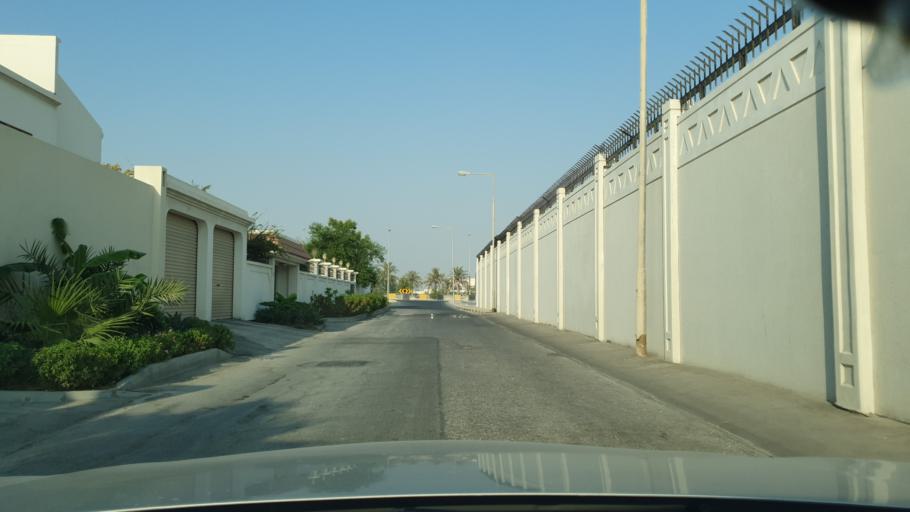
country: BH
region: Northern
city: Madinat `Isa
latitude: 26.1547
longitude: 50.5382
